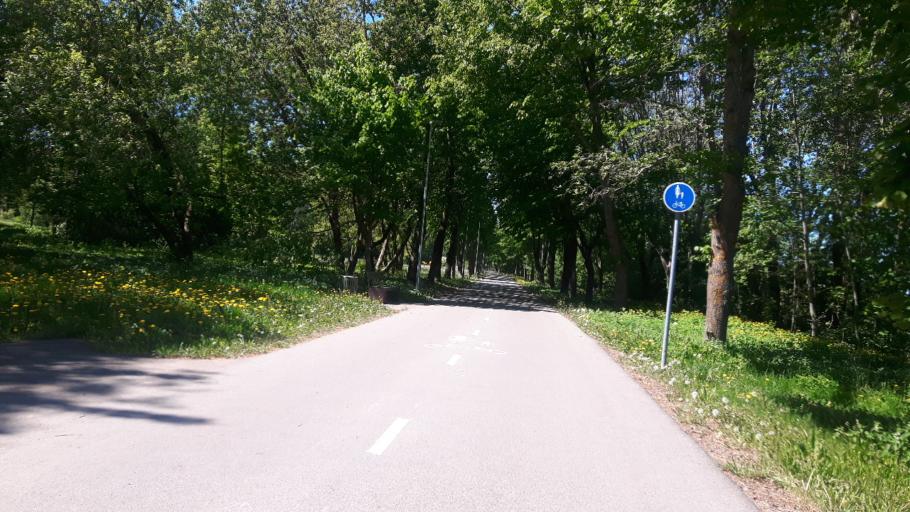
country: EE
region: Ida-Virumaa
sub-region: Sillamaee linn
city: Sillamae
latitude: 59.3963
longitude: 27.7859
